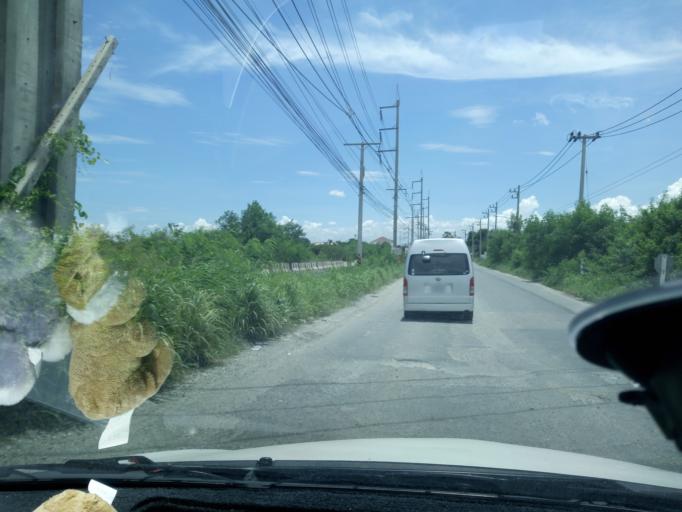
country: TH
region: Chon Buri
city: Phan Thong
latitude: 13.4265
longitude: 101.0632
